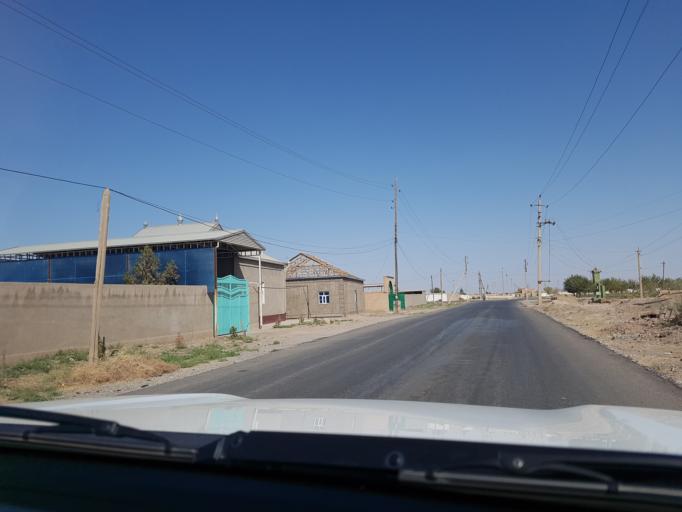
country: IR
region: Razavi Khorasan
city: Sarakhs
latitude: 36.5131
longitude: 61.2212
